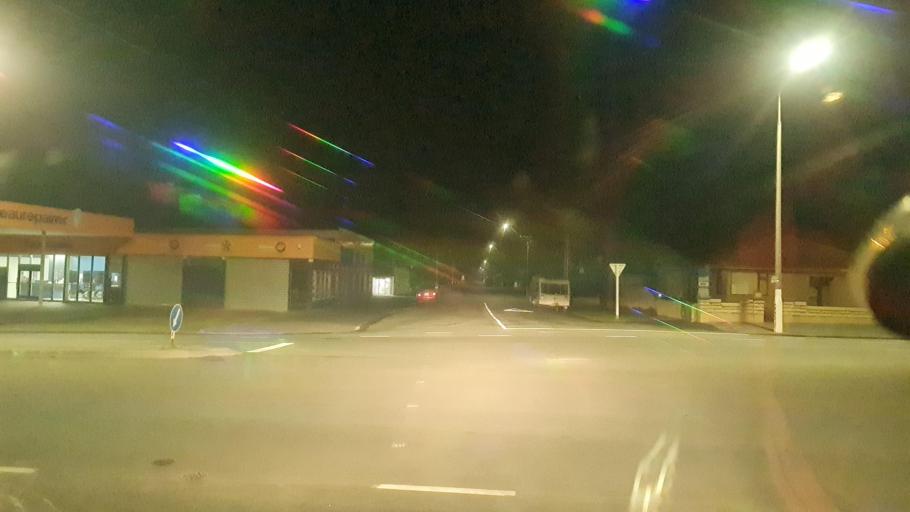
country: NZ
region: Otago
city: Oamaru
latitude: -45.0874
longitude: 170.9761
